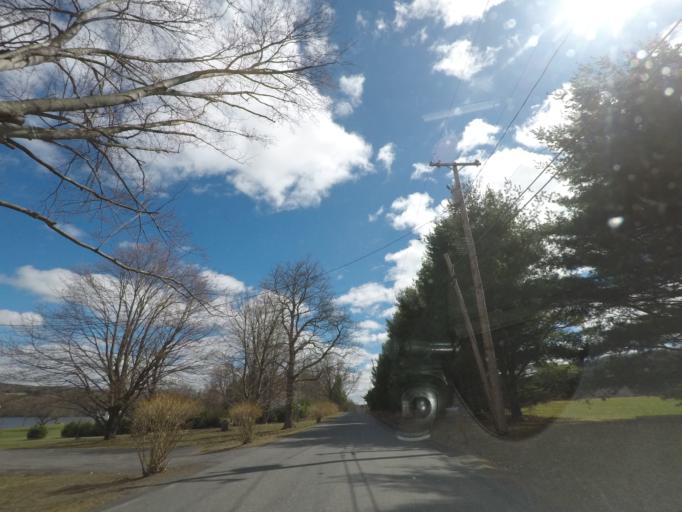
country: US
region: New York
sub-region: Albany County
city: Voorheesville
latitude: 42.6151
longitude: -73.9601
